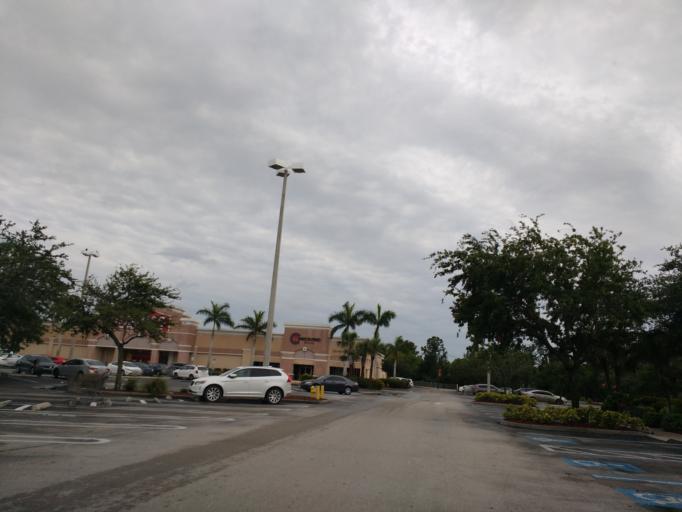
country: US
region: Florida
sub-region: Lee County
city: Villas
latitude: 26.5443
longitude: -81.8739
